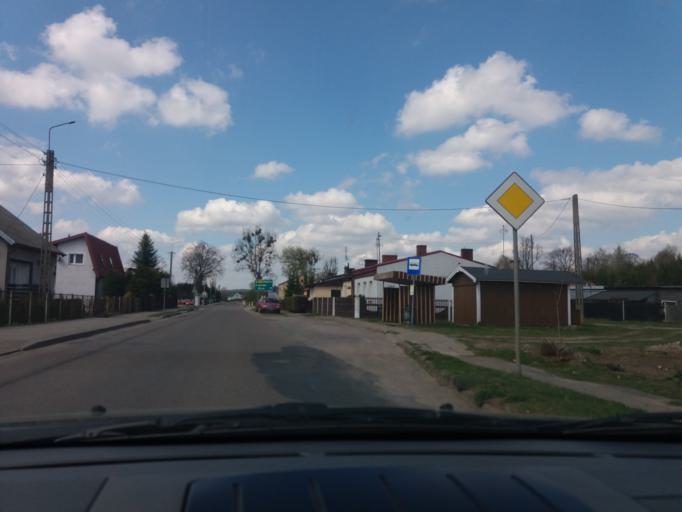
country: PL
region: Warmian-Masurian Voivodeship
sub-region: Powiat nidzicki
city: Nidzica
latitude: 53.3725
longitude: 20.6066
